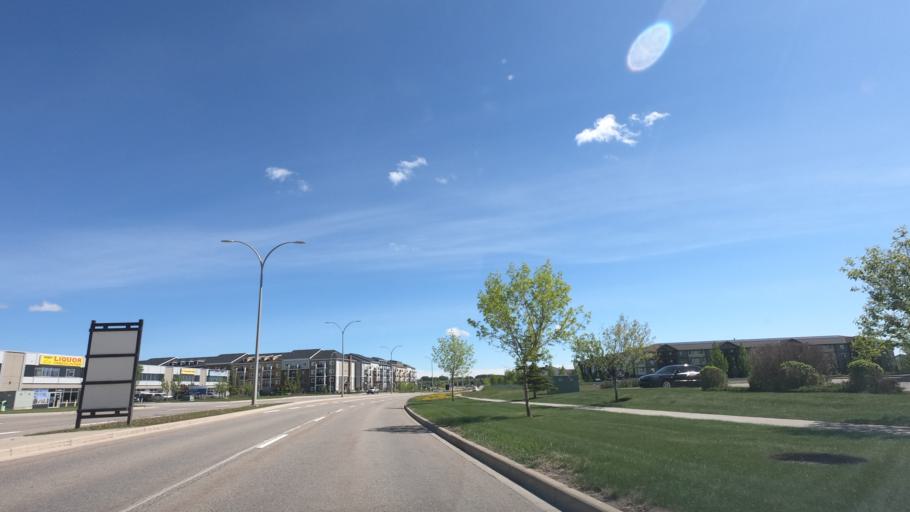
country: CA
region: Alberta
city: Airdrie
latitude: 51.2650
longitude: -113.9944
